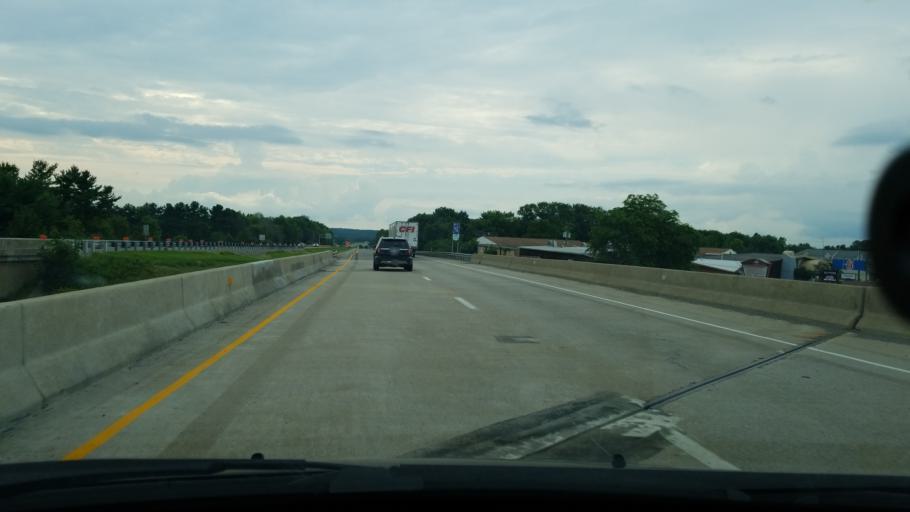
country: US
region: Ohio
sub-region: Mahoning County
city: Boardman
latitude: 40.9704
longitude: -80.6601
